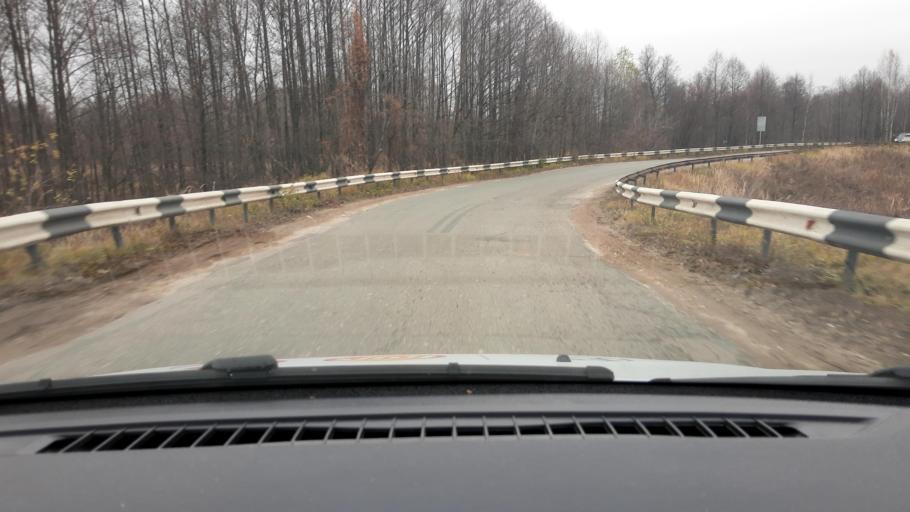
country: RU
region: Nizjnij Novgorod
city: Neklyudovo
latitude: 56.4233
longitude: 43.9250
